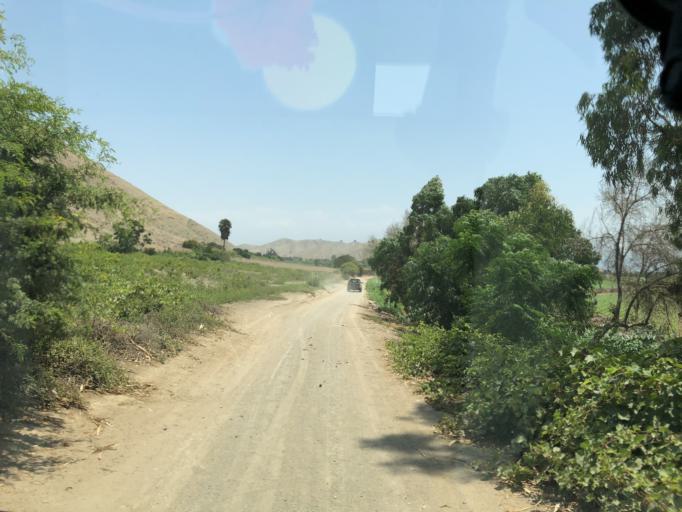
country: PE
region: Lima
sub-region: Provincia de Canete
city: Quilmana
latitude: -12.9773
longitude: -76.4270
